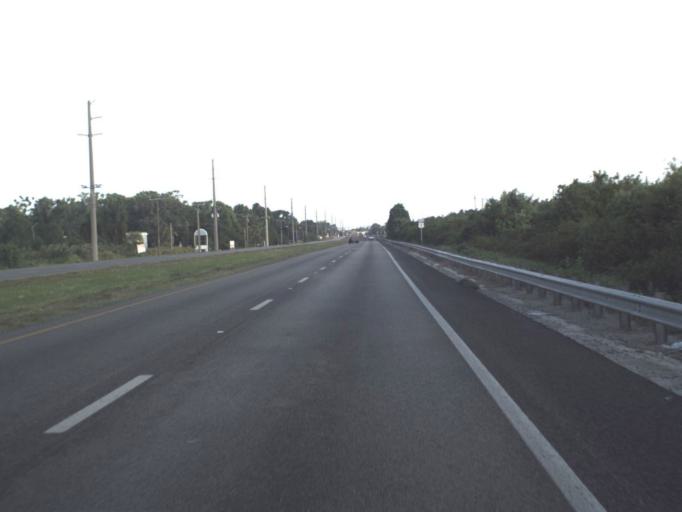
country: US
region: Florida
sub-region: Brevard County
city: Rockledge
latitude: 28.2681
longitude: -80.6906
